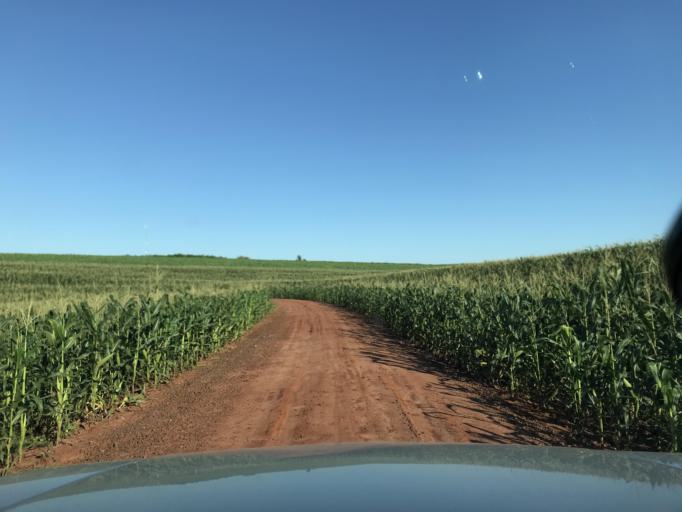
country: BR
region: Parana
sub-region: Palotina
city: Palotina
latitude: -24.2336
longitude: -53.7733
